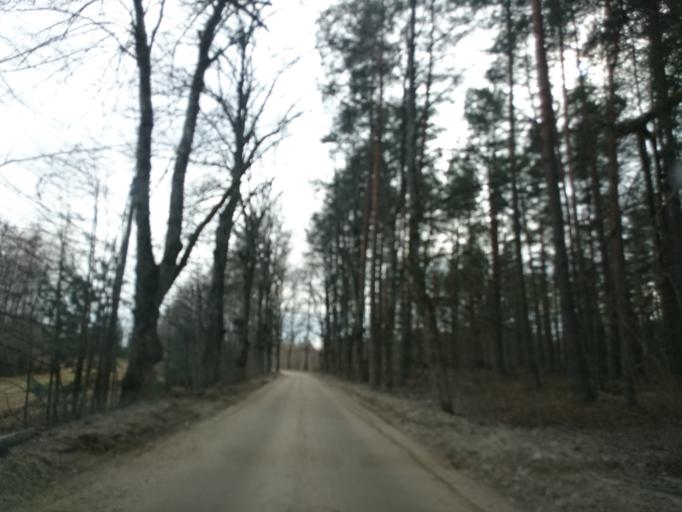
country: LV
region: Garkalne
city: Garkalne
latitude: 57.0192
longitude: 24.3866
